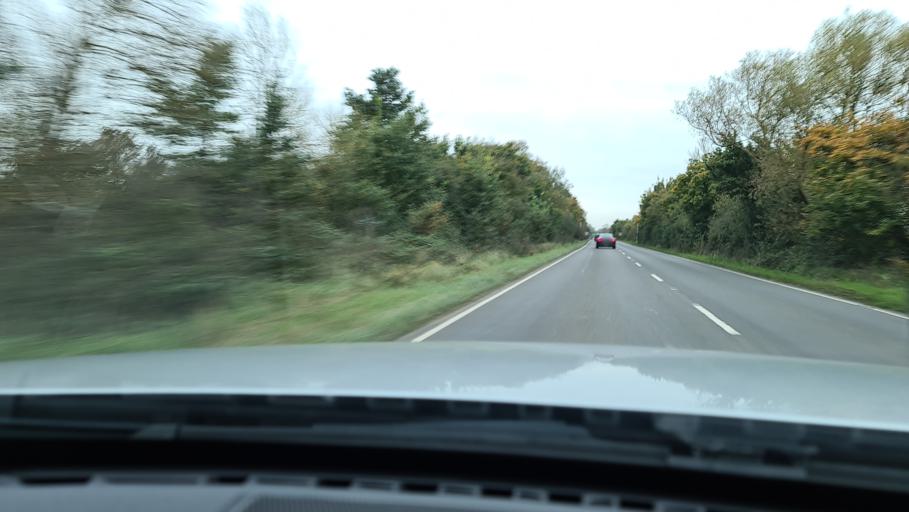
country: GB
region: England
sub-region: Oxfordshire
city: Bicester
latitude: 51.8760
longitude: -1.0847
